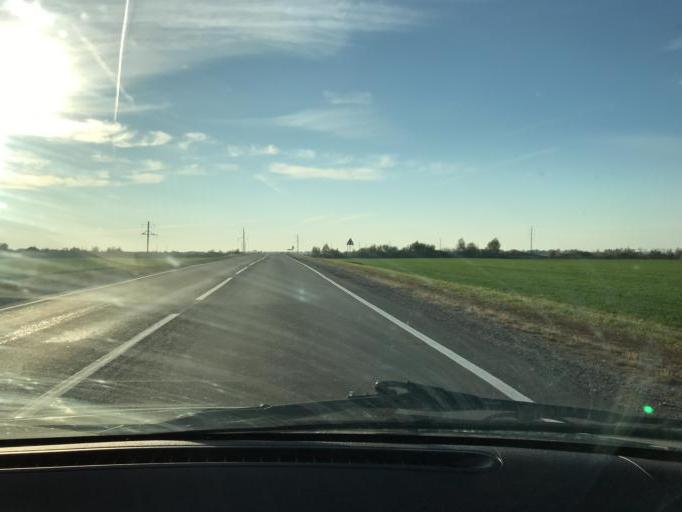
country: BY
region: Brest
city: Antopal'
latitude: 52.2193
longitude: 24.6819
